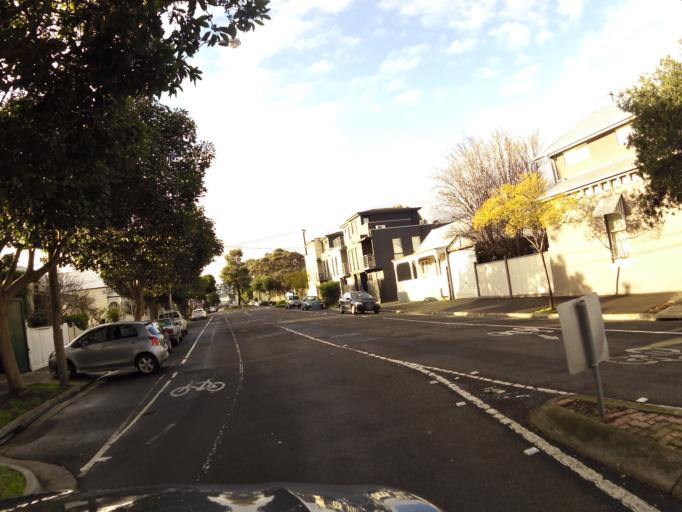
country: AU
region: Victoria
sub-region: Yarra
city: Richmond
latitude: -37.8159
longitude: 145.0058
